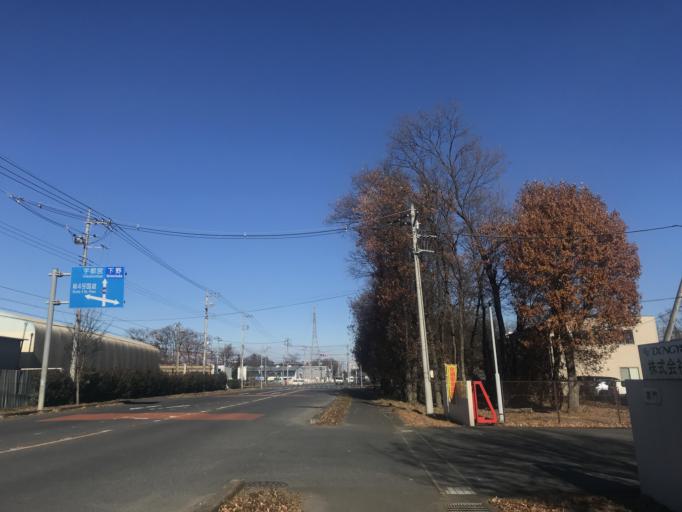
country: JP
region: Ibaraki
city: Yuki
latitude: 36.3277
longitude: 139.8799
